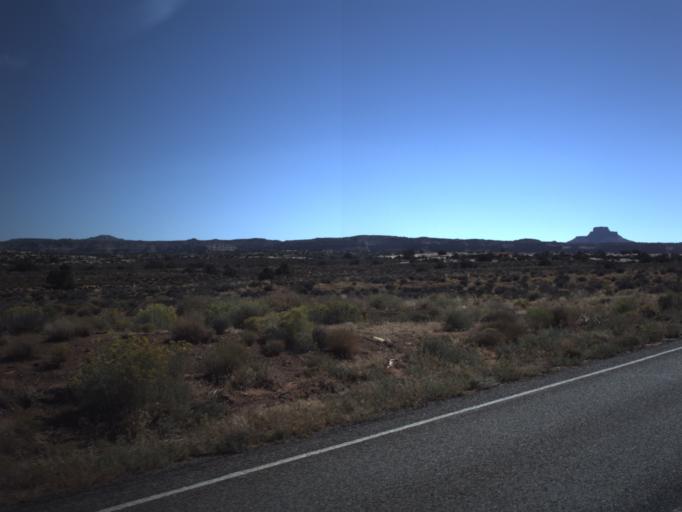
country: US
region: Utah
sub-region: San Juan County
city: Blanding
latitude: 37.7947
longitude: -110.3022
